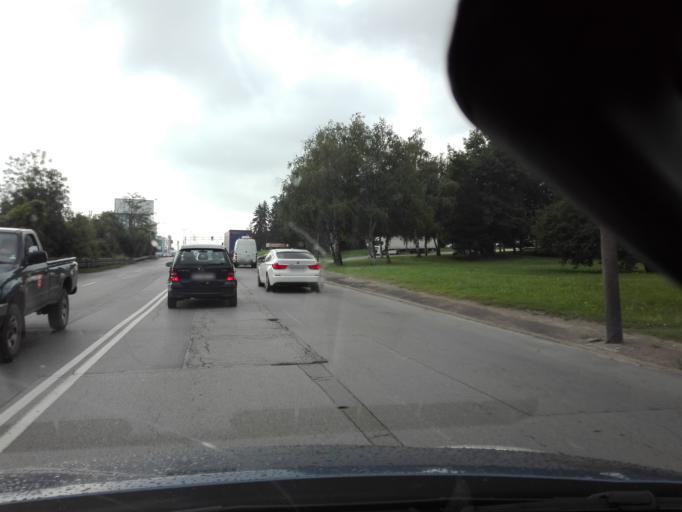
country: BG
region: Sofia-Capital
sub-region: Stolichna Obshtina
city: Sofia
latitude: 42.6585
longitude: 23.2695
